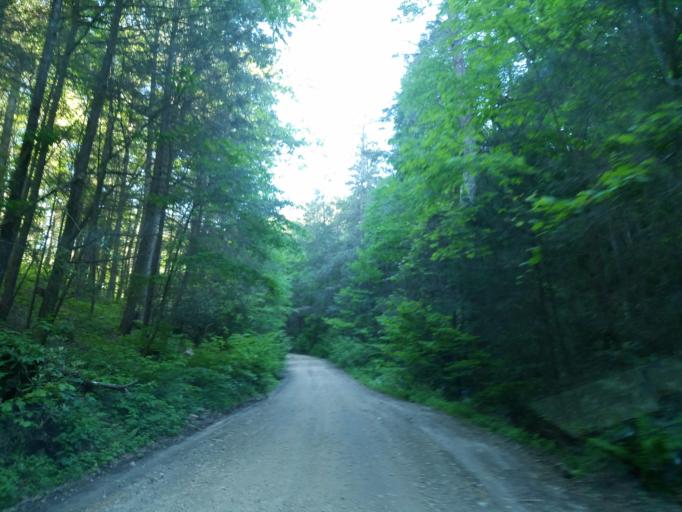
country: US
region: Georgia
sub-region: Fannin County
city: Blue Ridge
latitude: 34.7025
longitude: -84.1505
